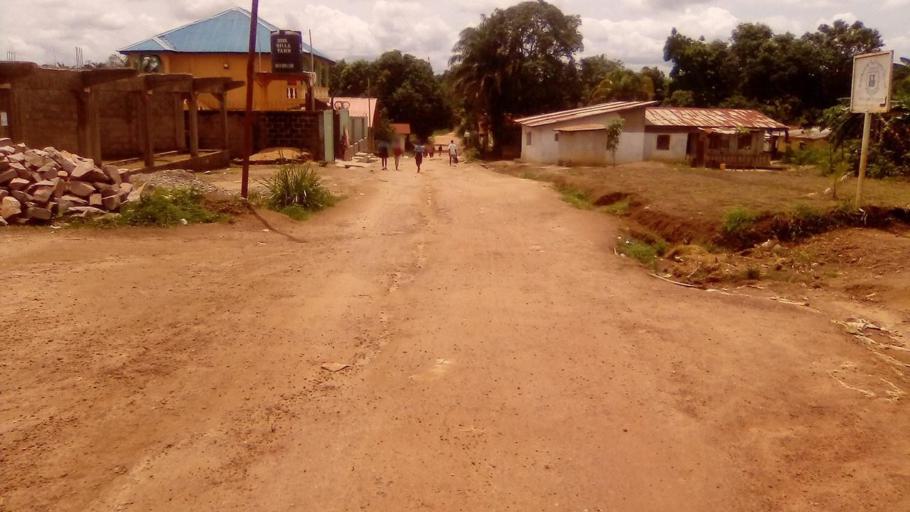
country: SL
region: Southern Province
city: Bo
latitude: 7.9396
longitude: -11.7368
